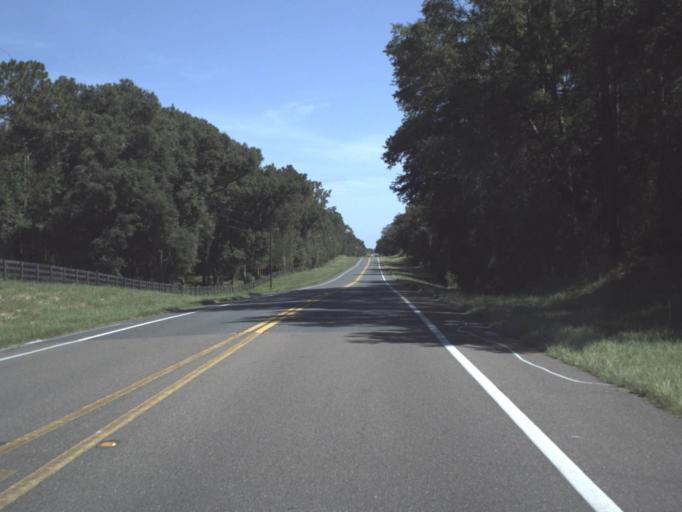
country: US
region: Florida
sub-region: Levy County
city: Williston
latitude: 29.2877
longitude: -82.4460
